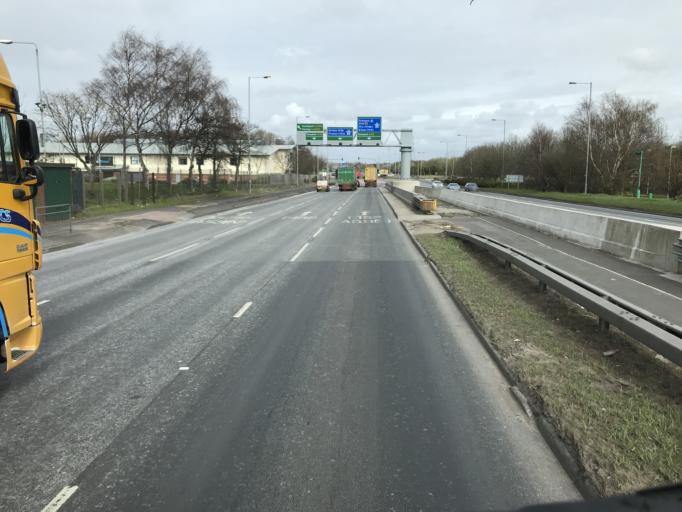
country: GB
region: England
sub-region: Sefton
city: Maghull
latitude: 53.4901
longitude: -2.9557
